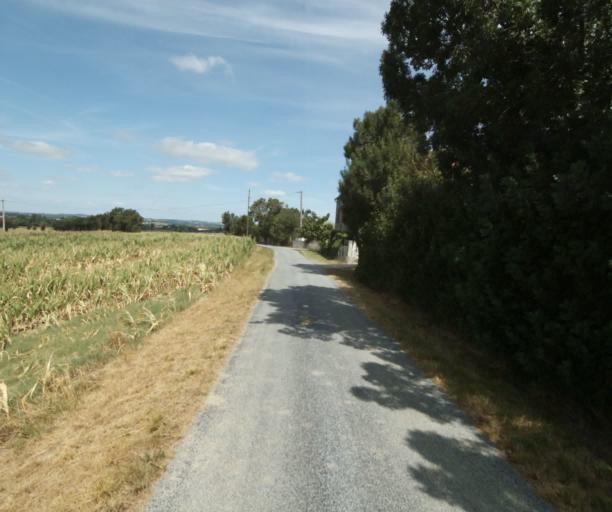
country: FR
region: Midi-Pyrenees
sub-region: Departement du Tarn
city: Dourgne
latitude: 43.4934
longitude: 2.0954
